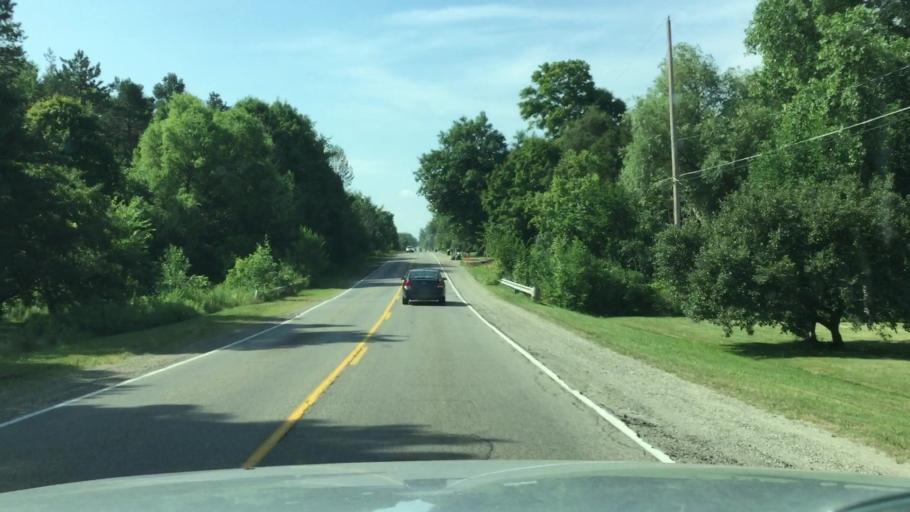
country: US
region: Michigan
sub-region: Genesee County
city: Flushing
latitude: 43.0983
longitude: -83.8136
